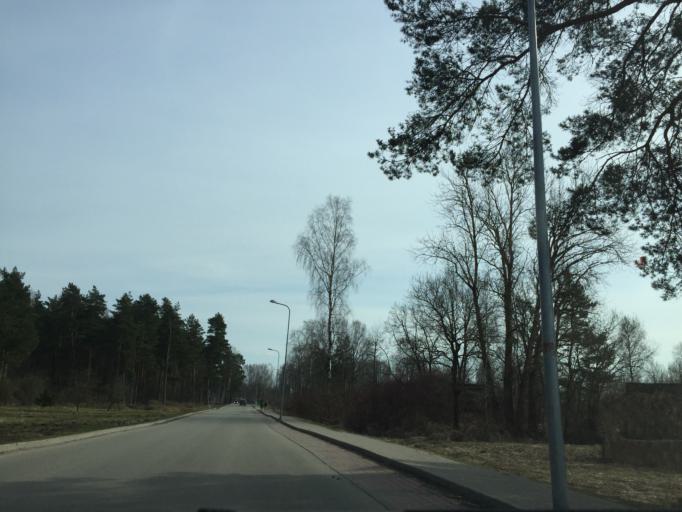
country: LV
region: Kekava
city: Balozi
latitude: 56.8753
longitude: 24.1255
